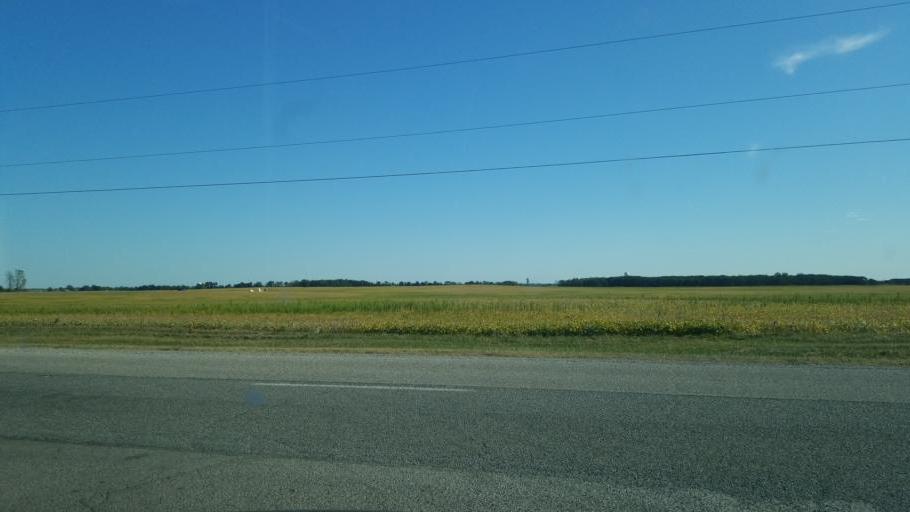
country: US
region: Ohio
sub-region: Madison County
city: Choctaw Lake
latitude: 39.9350
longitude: -83.4729
